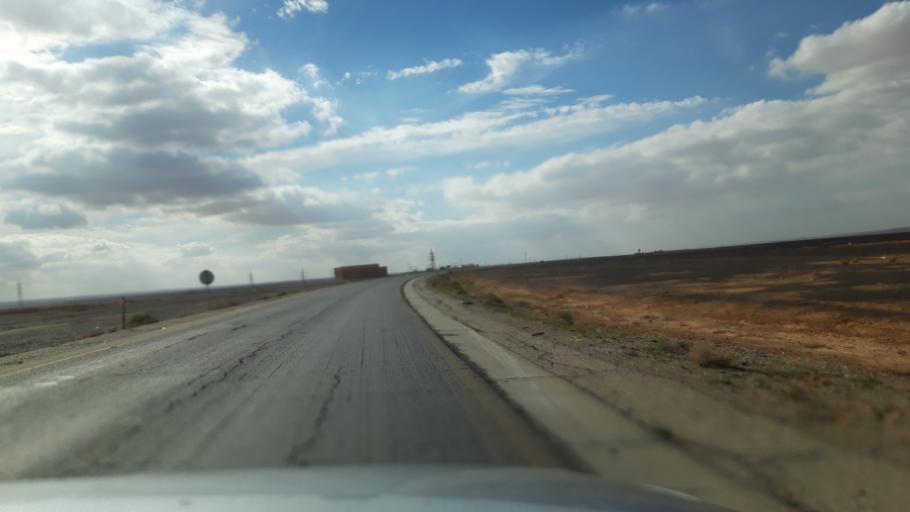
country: JO
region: Amman
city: Al Azraq ash Shamali
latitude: 31.7286
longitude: 36.4685
